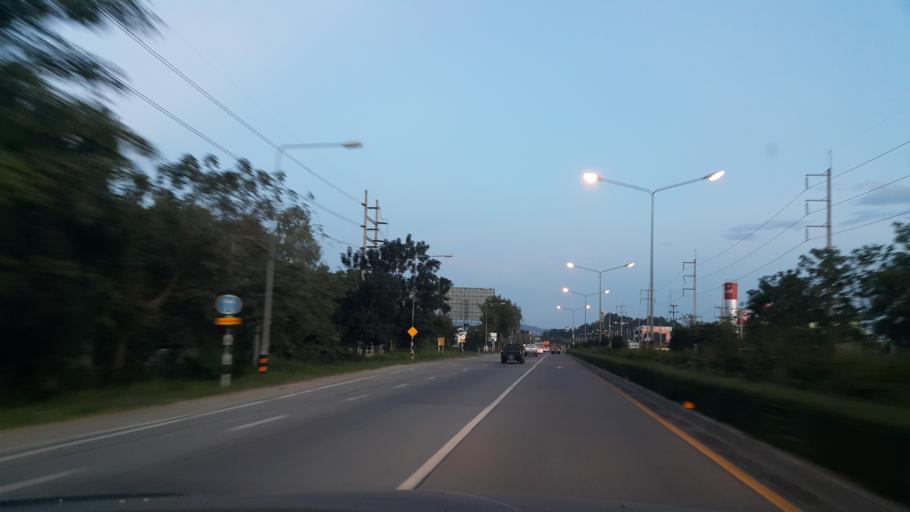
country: TH
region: Lamphun
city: Lamphun
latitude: 18.5548
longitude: 99.0443
